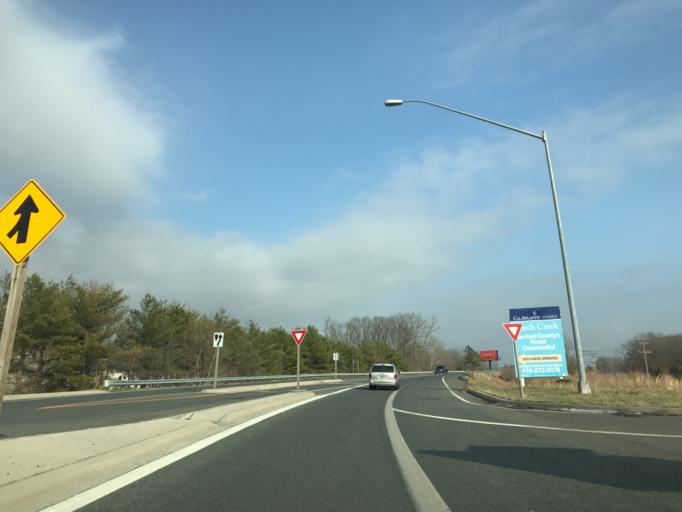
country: US
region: Maryland
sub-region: Harford County
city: Perryman
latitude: 39.4919
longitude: -76.2059
